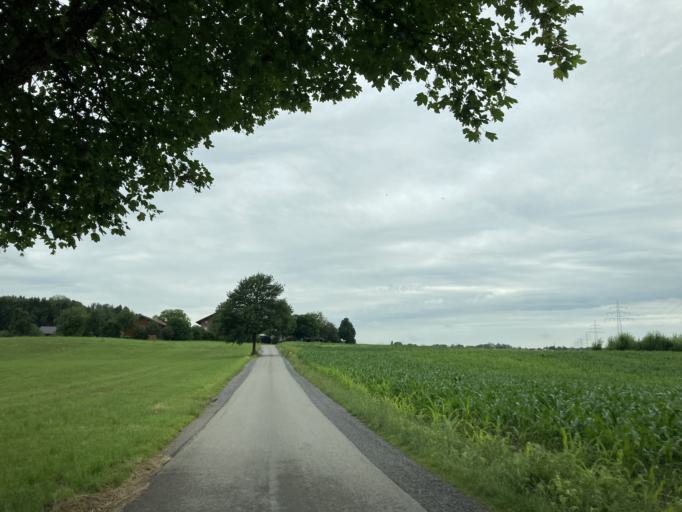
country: DE
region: Bavaria
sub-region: Upper Bavaria
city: Stephanskirchen
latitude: 47.8643
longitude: 12.1874
